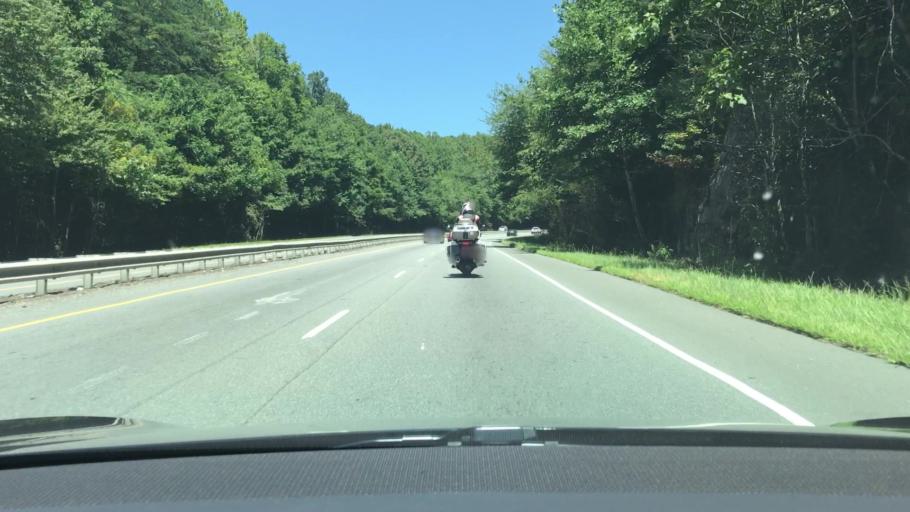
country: US
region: North Carolina
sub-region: Jackson County
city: Sylva
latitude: 35.3706
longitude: -83.2537
